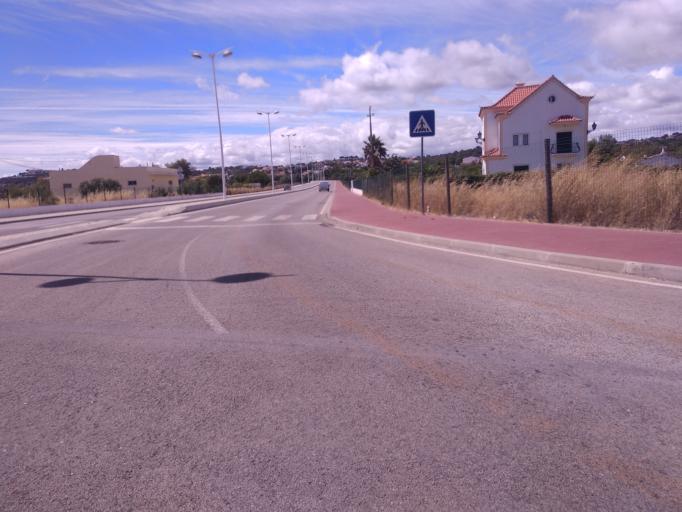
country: PT
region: Faro
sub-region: Sao Bras de Alportel
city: Sao Bras de Alportel
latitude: 37.1542
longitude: -7.8763
